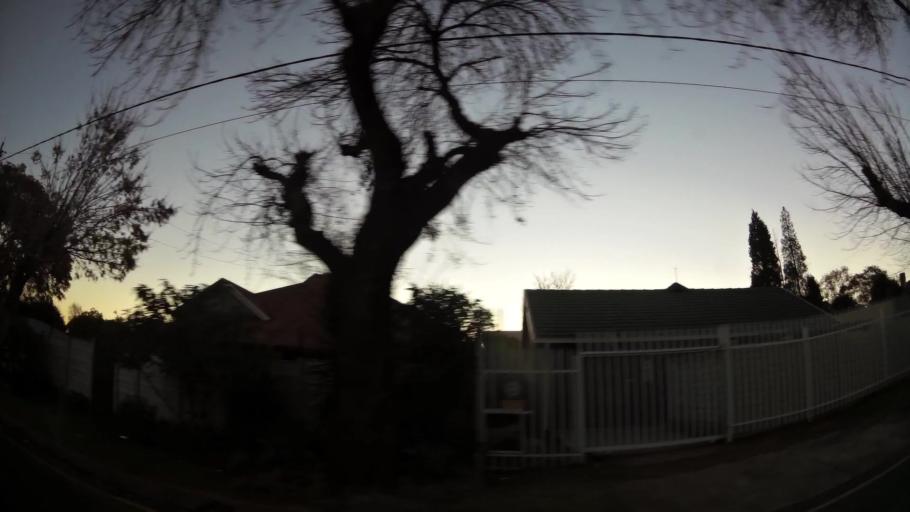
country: ZA
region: Gauteng
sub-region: City of Johannesburg Metropolitan Municipality
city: Roodepoort
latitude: -26.1738
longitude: 27.9146
